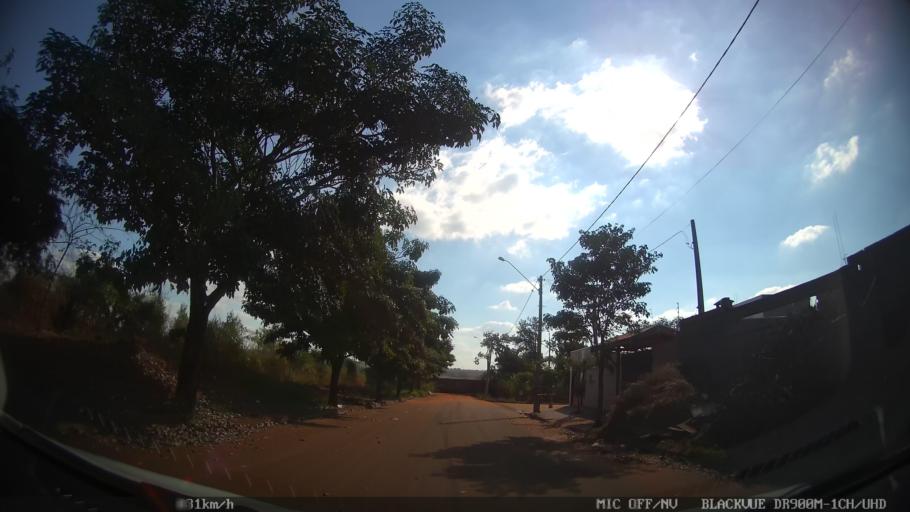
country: BR
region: Sao Paulo
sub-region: Sumare
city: Sumare
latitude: -22.8222
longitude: -47.2966
